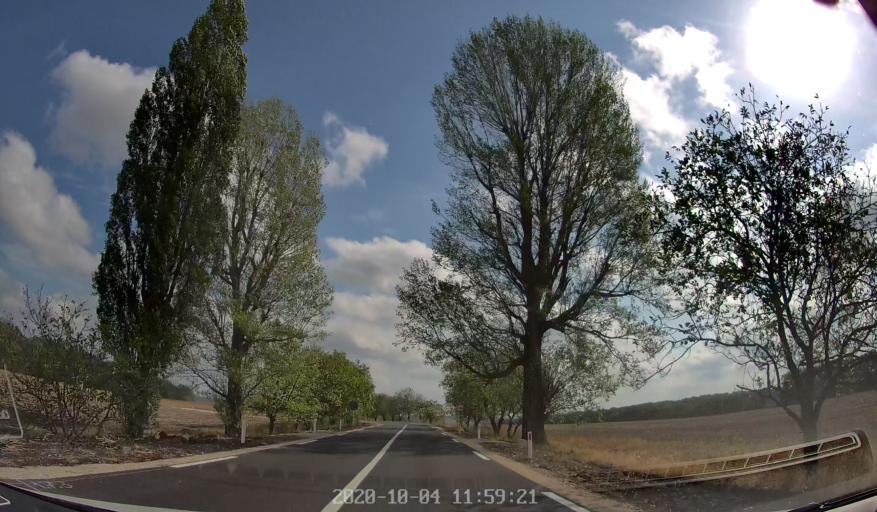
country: MD
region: Rezina
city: Saharna
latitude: 47.6321
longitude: 28.8495
